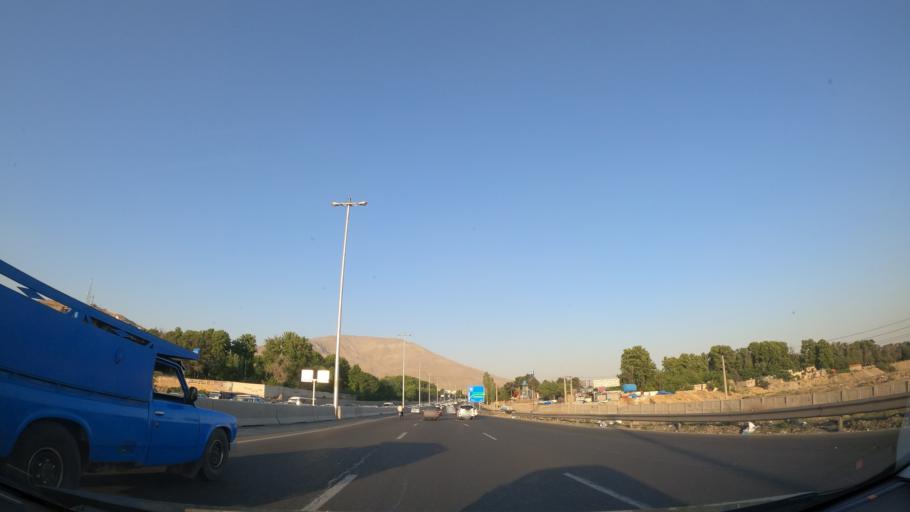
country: IR
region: Alborz
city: Karaj
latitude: 35.7902
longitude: 51.0098
